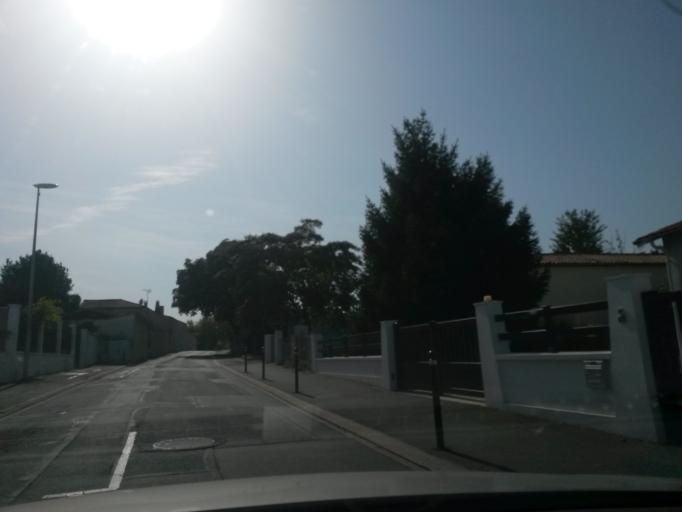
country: FR
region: Poitou-Charentes
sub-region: Departement de la Charente-Maritime
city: Saint-Xandre
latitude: 46.2028
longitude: -1.1014
